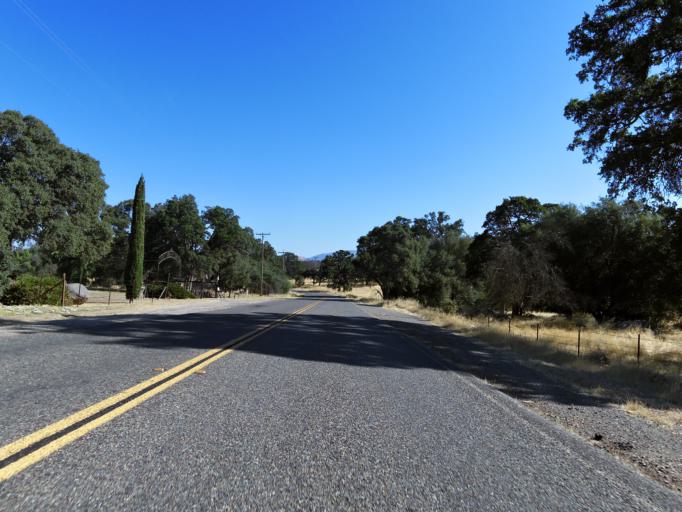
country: US
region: California
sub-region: Mariposa County
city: Mariposa
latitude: 37.4445
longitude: -120.1027
